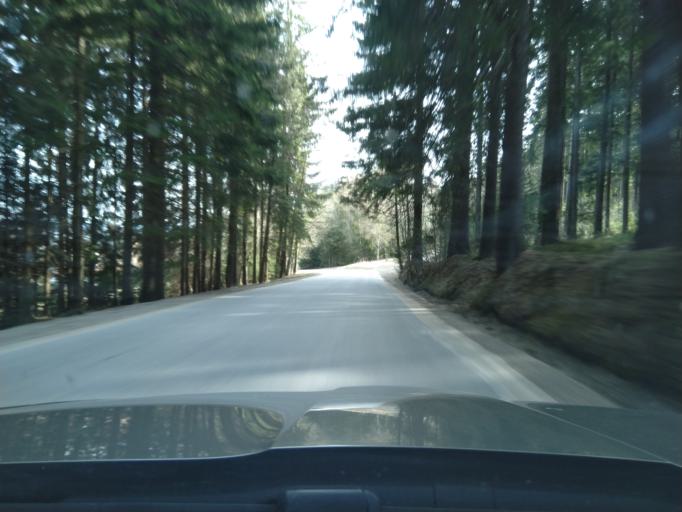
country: CZ
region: Jihocesky
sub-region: Okres Prachatice
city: Stachy
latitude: 49.0717
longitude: 13.6504
